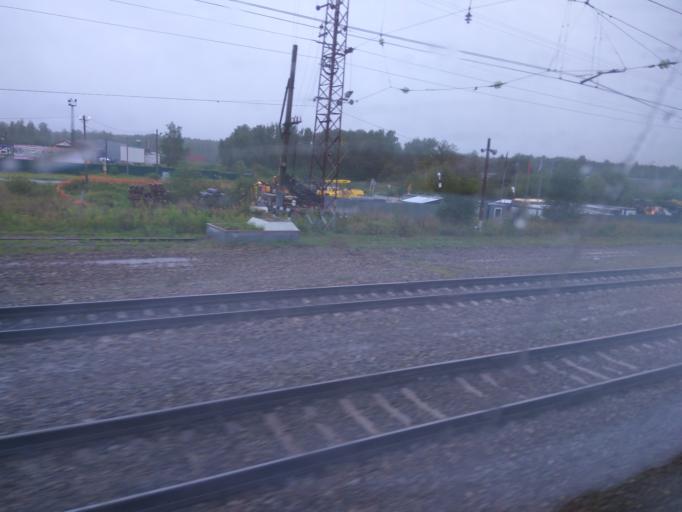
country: RU
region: Moskovskaya
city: Zhilevo
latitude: 54.9918
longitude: 38.0284
